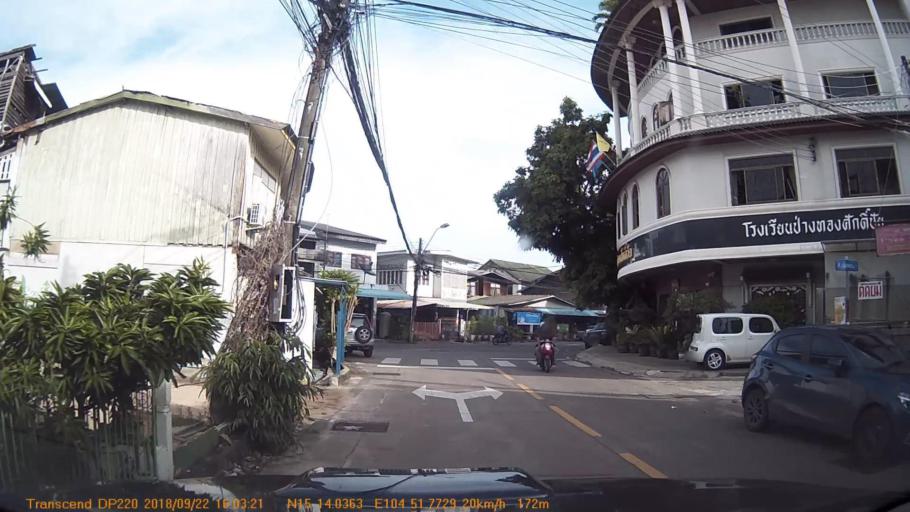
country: TH
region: Changwat Ubon Ratchathani
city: Ubon Ratchathani
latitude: 15.2338
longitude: 104.8629
